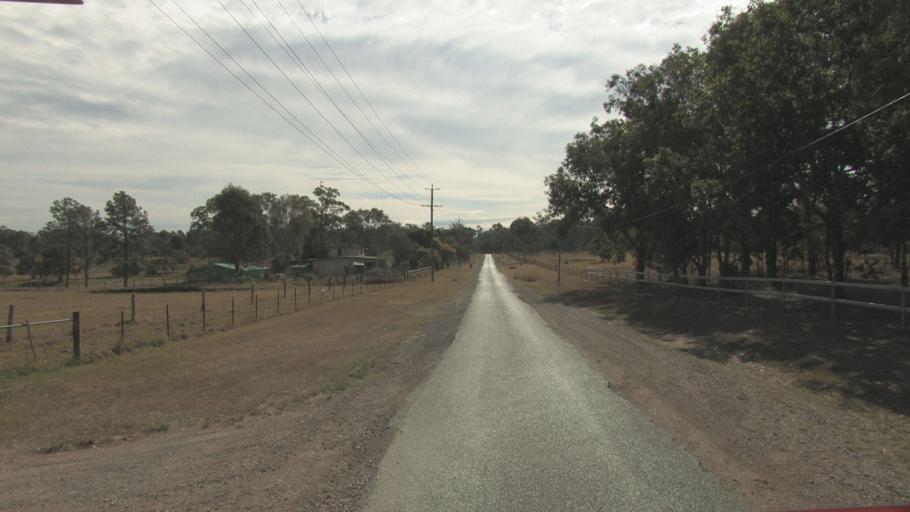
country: AU
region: Queensland
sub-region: Logan
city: North Maclean
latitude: -27.7793
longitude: 153.0078
